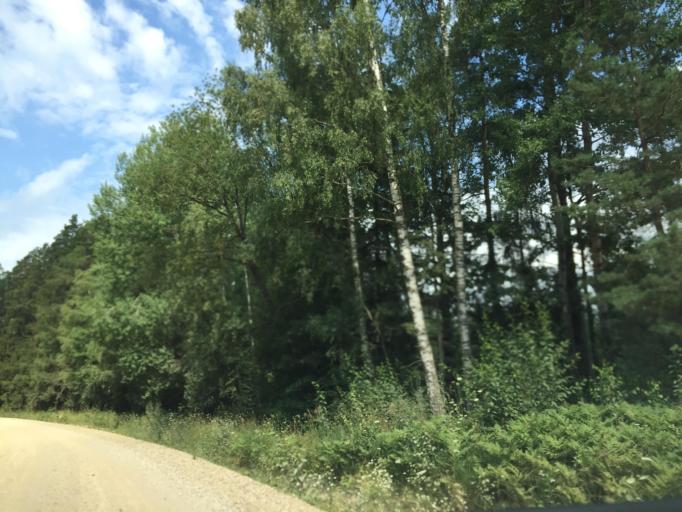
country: LV
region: Kandava
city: Kandava
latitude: 57.0078
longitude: 22.8430
